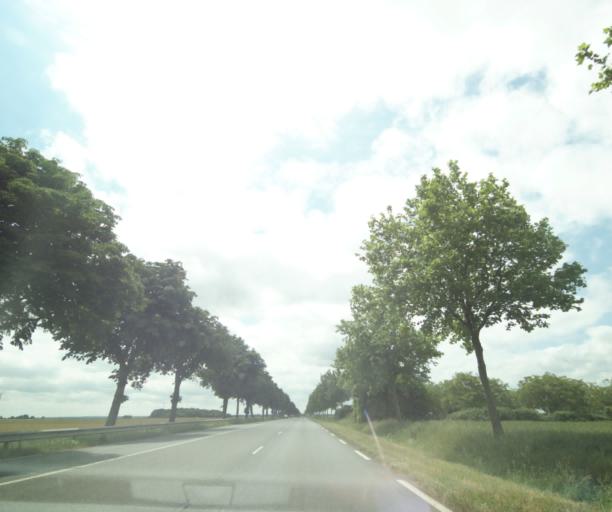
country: FR
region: Poitou-Charentes
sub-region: Departement des Deux-Sevres
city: Saint-Jean-de-Thouars
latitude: 46.9473
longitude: -0.2050
